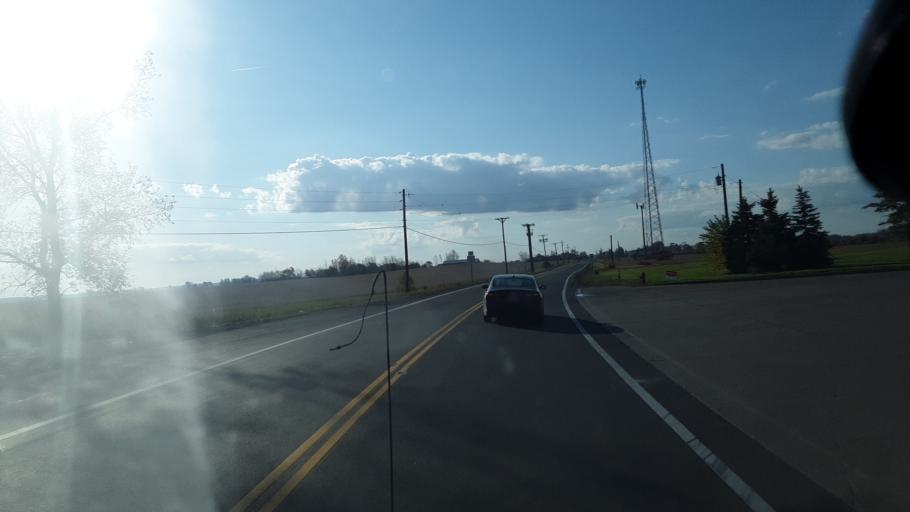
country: US
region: Ohio
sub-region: Fayette County
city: Jeffersonville
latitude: 39.6462
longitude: -83.5367
